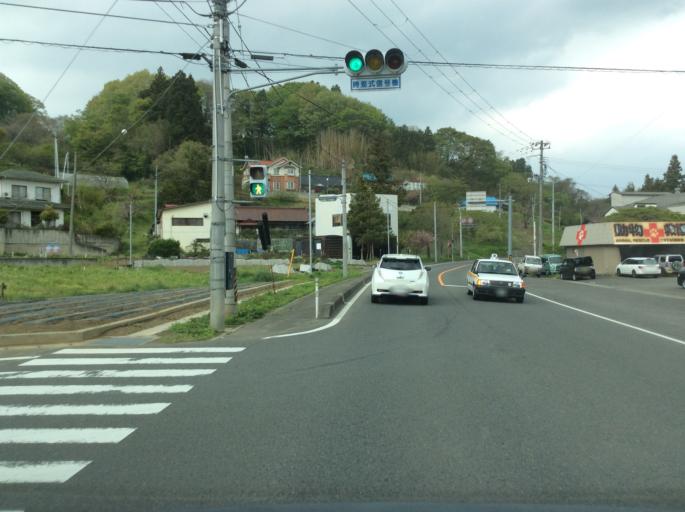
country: JP
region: Fukushima
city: Miharu
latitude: 37.4274
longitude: 140.4571
